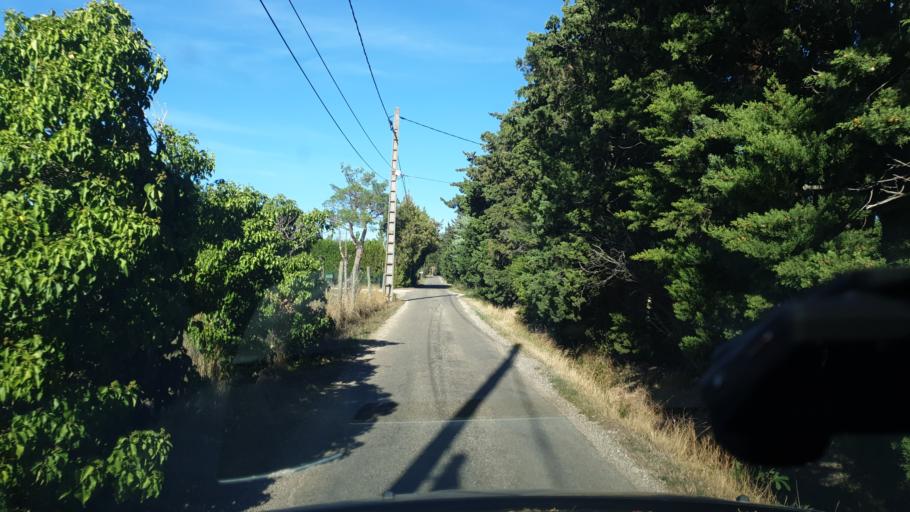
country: FR
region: Provence-Alpes-Cote d'Azur
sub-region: Departement du Vaucluse
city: Monteux
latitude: 44.0464
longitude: 5.0130
